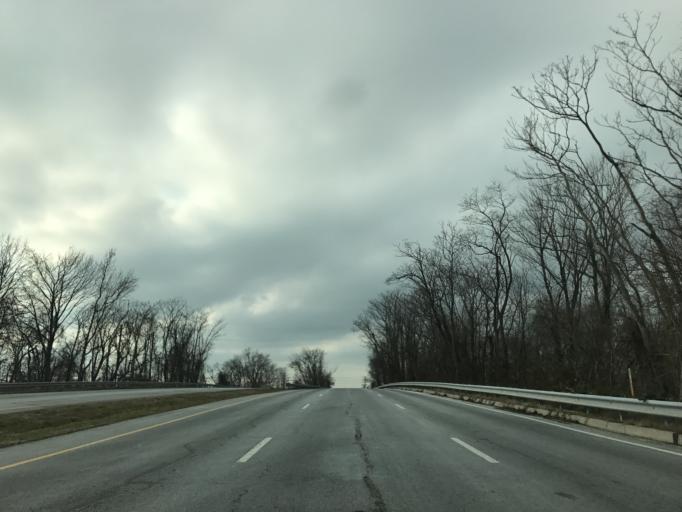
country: US
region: Maryland
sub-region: Harford County
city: Aberdeen
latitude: 39.4901
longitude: -76.1735
